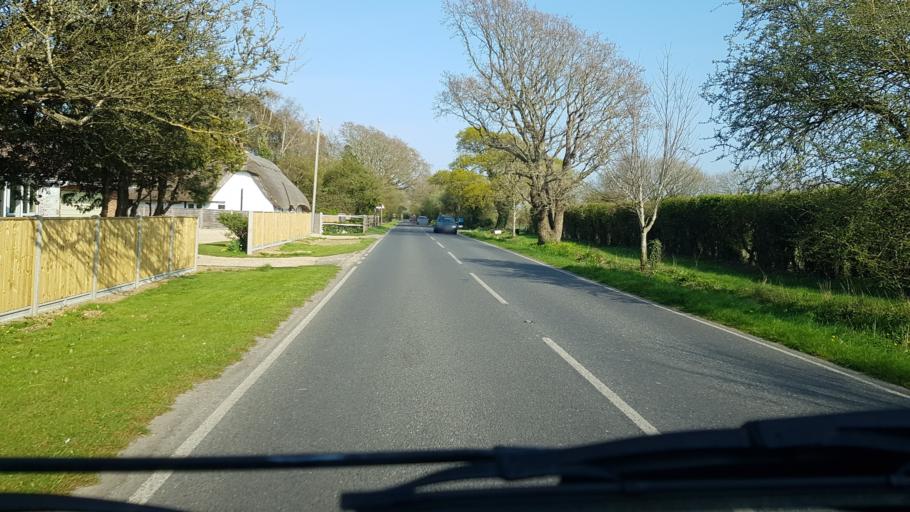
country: GB
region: England
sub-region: West Sussex
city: East Wittering
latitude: 50.7871
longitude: -0.8554
